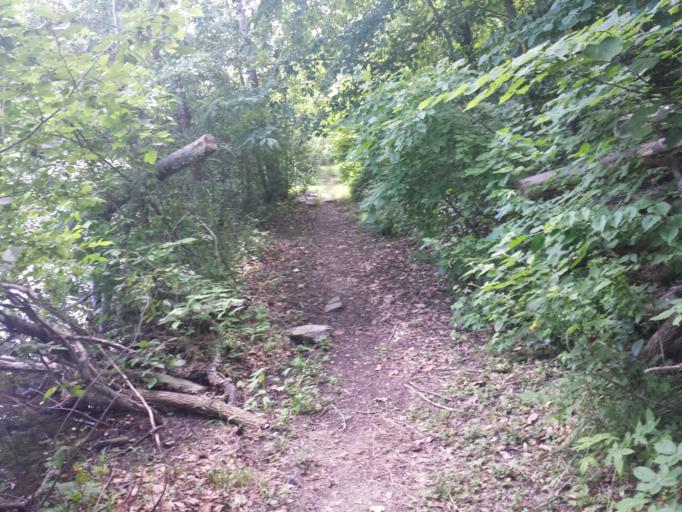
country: US
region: Virginia
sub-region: Prince William County
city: Montclair
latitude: 38.6179
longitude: -77.3565
